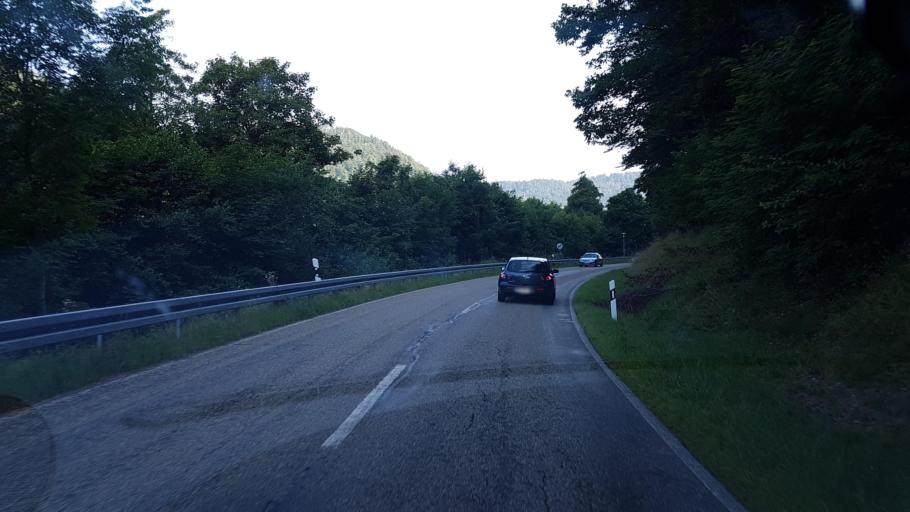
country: DE
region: Baden-Wuerttemberg
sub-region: Freiburg Region
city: Dachsberg
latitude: 47.7032
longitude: 8.1247
